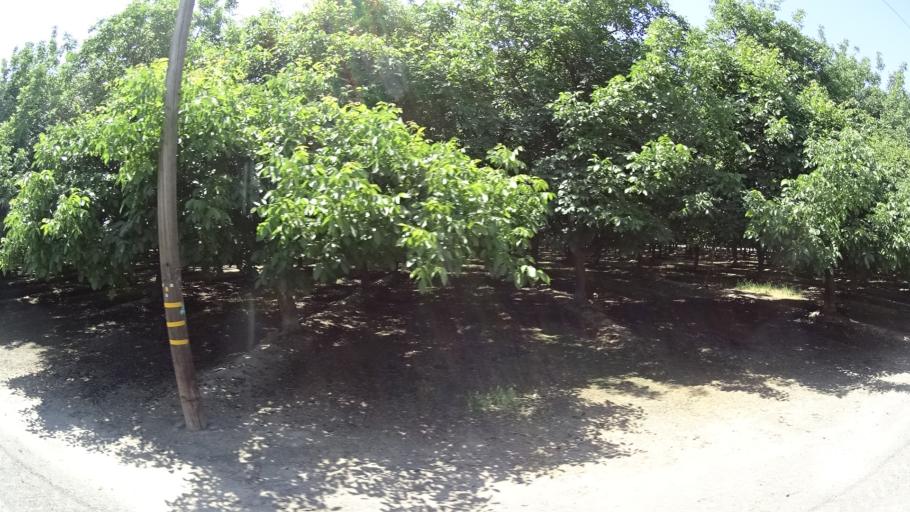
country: US
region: California
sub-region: Kings County
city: Lucerne
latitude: 36.4012
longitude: -119.6141
